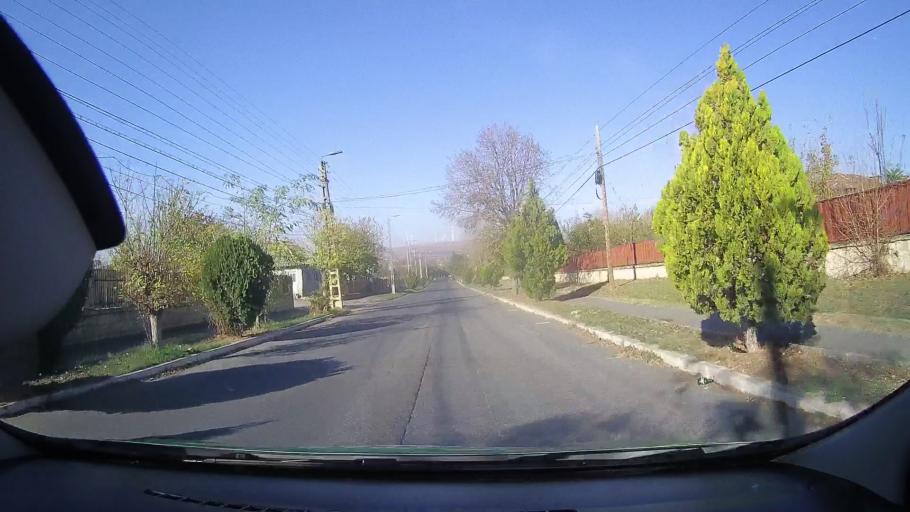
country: RO
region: Tulcea
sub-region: Oras Babadag
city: Babadag
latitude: 44.8884
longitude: 28.7314
